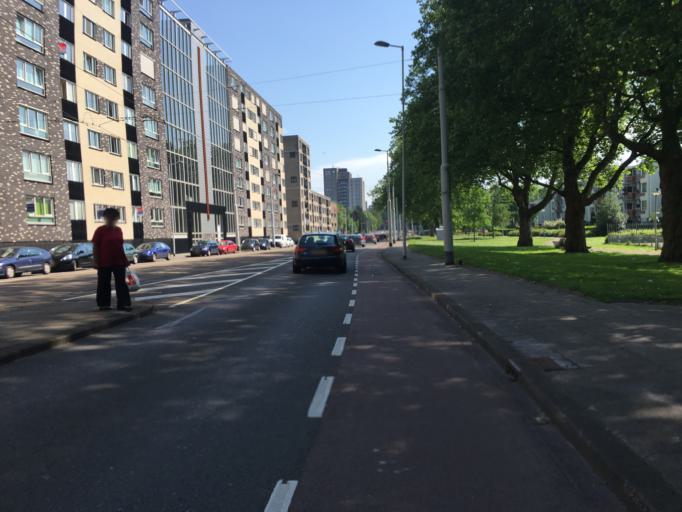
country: NL
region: South Holland
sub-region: Gemeente Rotterdam
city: Rotterdam
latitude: 51.9281
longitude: 4.4963
